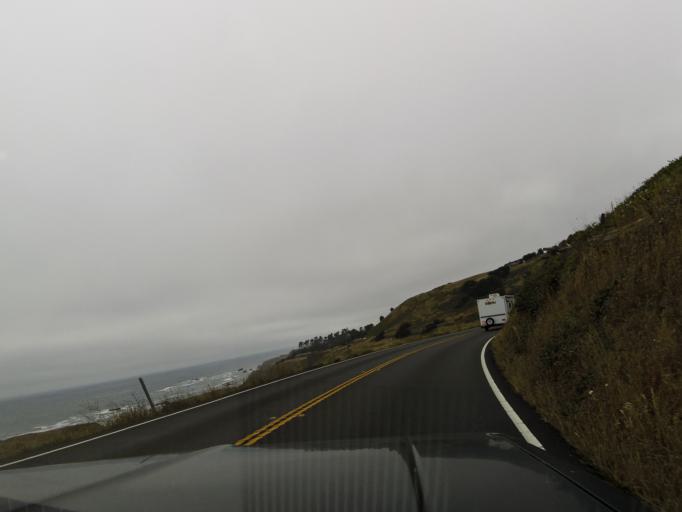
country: US
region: California
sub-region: Mendocino County
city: Fort Bragg
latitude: 39.1970
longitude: -123.7675
